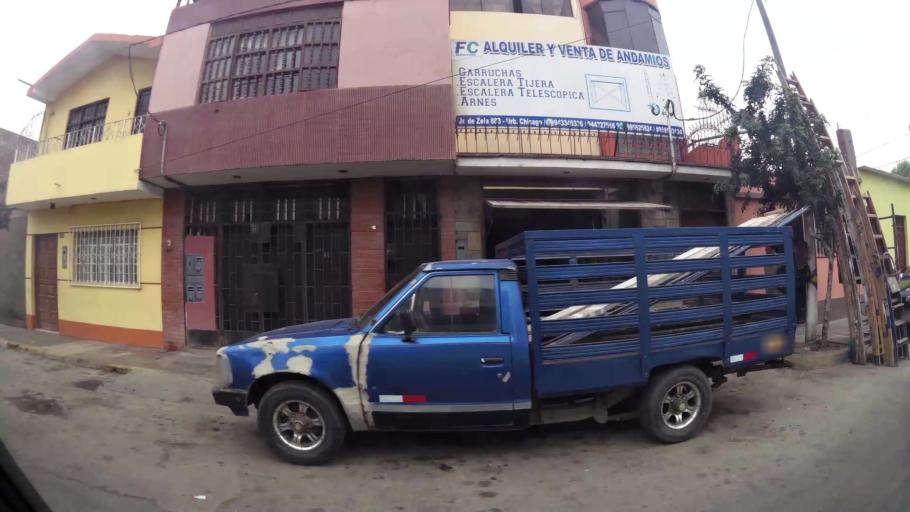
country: PE
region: La Libertad
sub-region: Provincia de Trujillo
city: Trujillo
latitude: -8.1164
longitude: -79.0167
